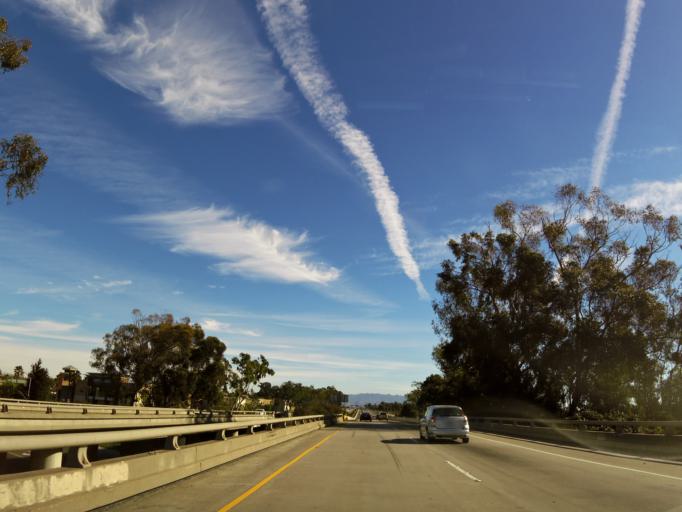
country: US
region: California
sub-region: Ventura County
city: Ventura
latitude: 34.2625
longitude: -119.2315
